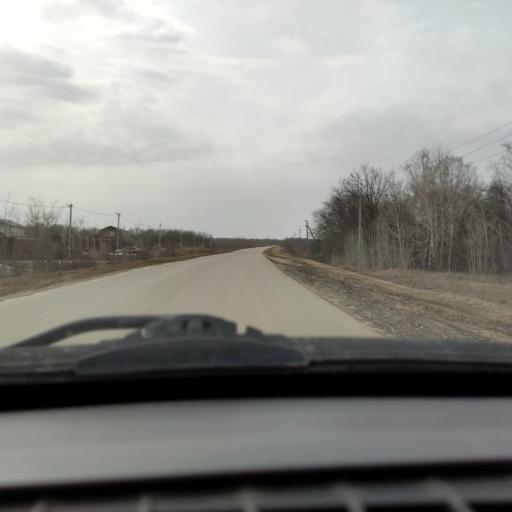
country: RU
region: Samara
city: Dubovyy Umet
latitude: 53.0377
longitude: 50.1723
